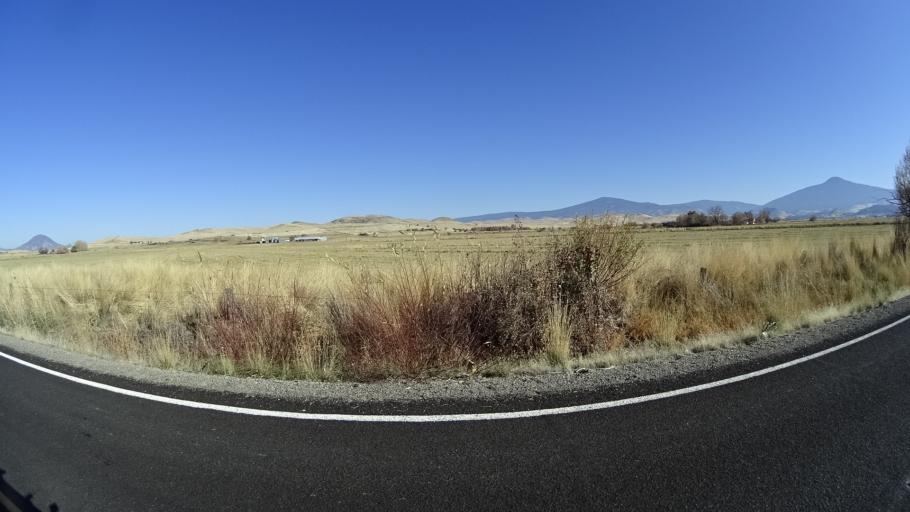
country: US
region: California
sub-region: Siskiyou County
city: Montague
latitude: 41.7150
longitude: -122.4434
